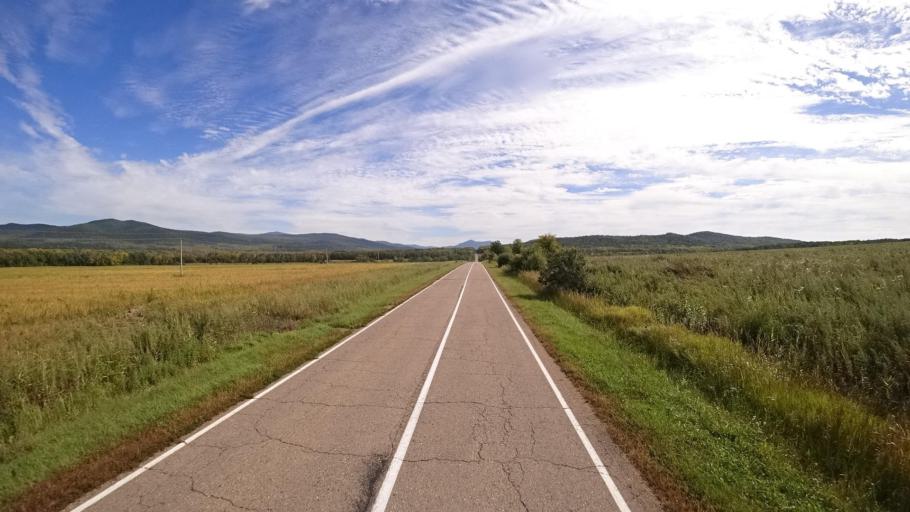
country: RU
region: Primorskiy
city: Yakovlevka
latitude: 44.4151
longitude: 133.5842
